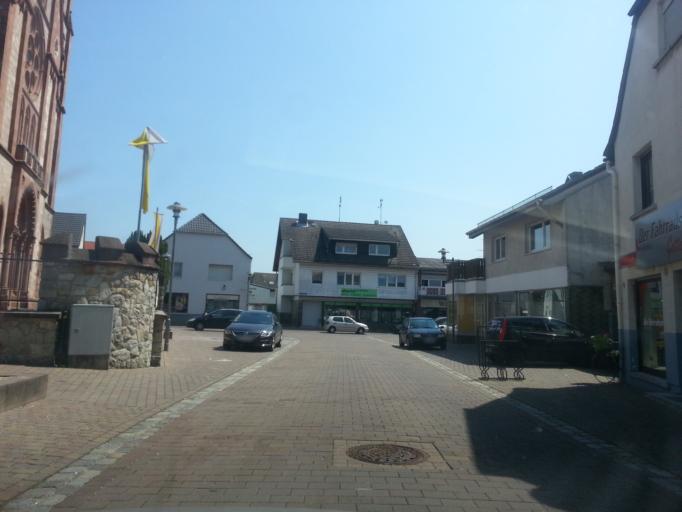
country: DE
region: Hesse
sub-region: Regierungsbezirk Darmstadt
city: Eppertshausen
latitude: 49.9782
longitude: 8.8270
